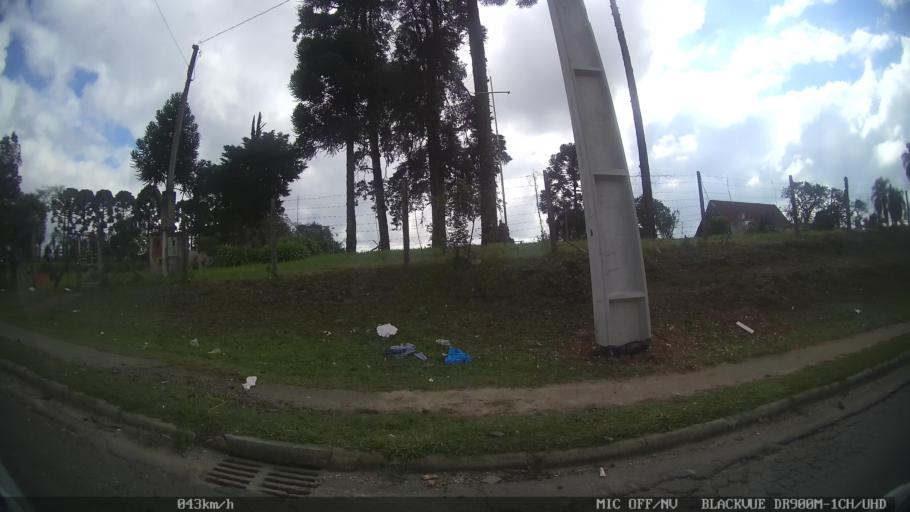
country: BR
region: Parana
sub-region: Colombo
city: Colombo
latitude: -25.3441
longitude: -49.1874
